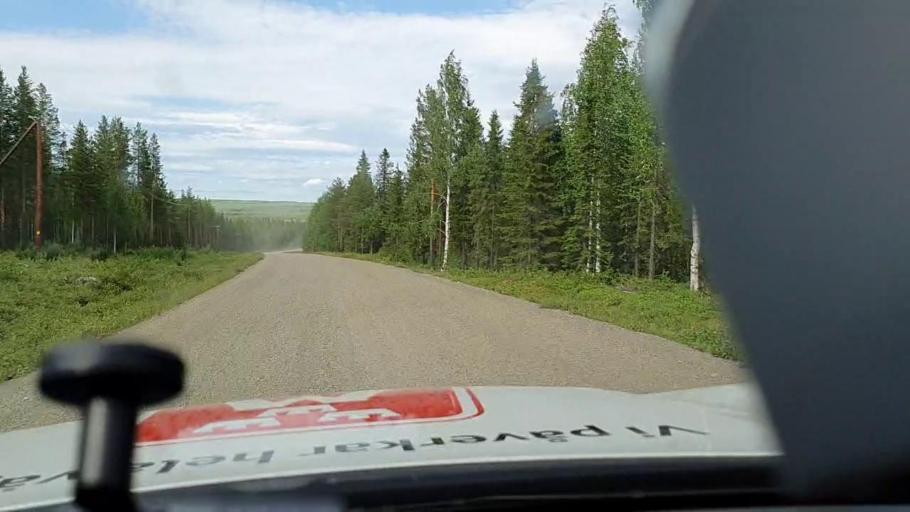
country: SE
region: Norrbotten
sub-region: Alvsbyns Kommun
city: AElvsbyn
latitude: 66.1425
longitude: 21.0174
